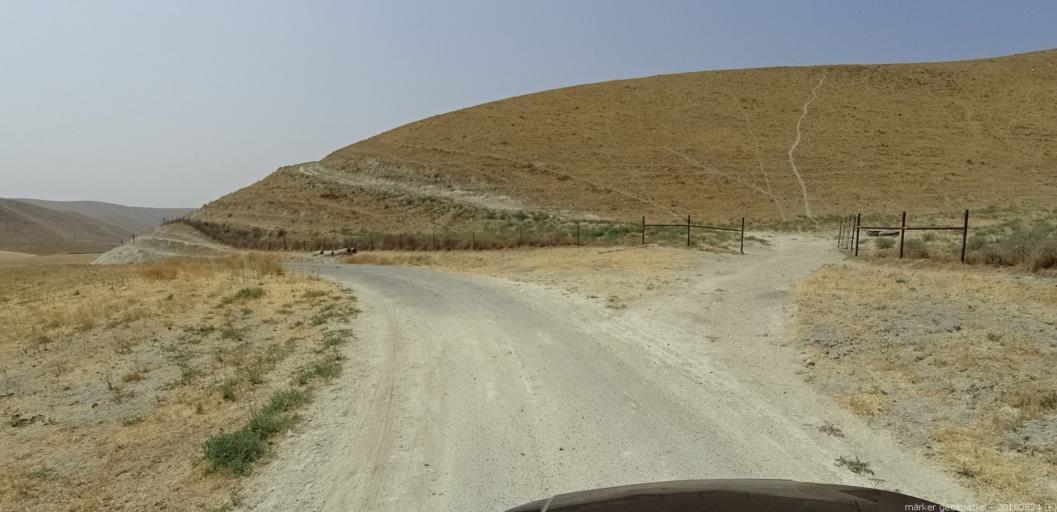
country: US
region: California
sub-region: Monterey County
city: King City
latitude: 36.2010
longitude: -120.9450
